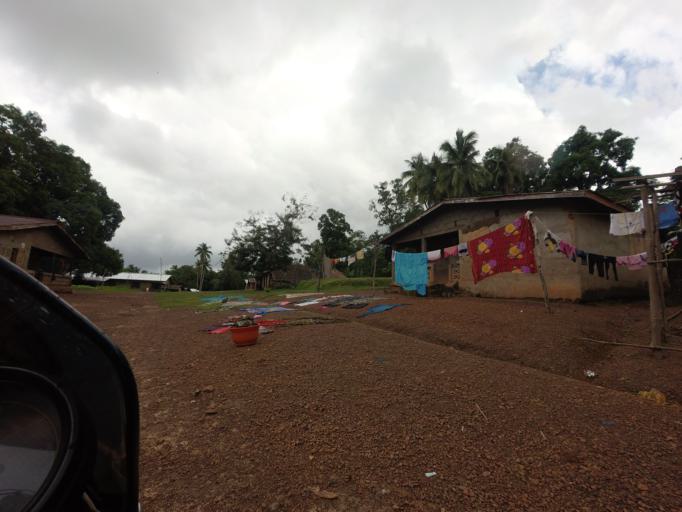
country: SL
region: Northern Province
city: Mambolo
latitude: 8.9722
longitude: -12.9969
